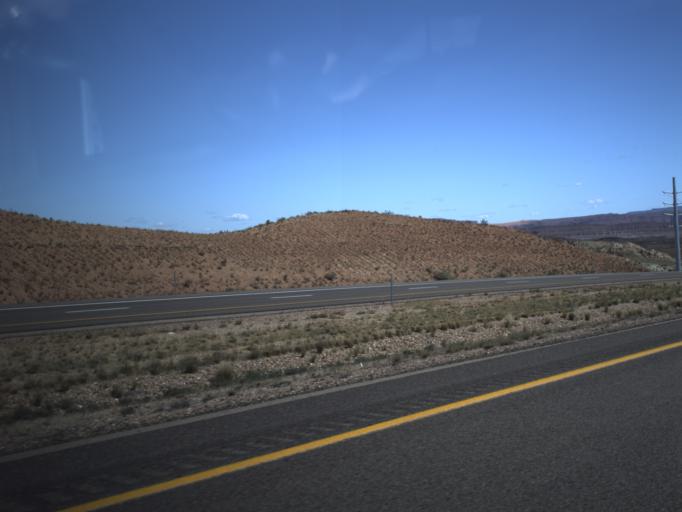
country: US
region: Utah
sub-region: Washington County
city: Saint George
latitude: 37.0051
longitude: -113.5366
